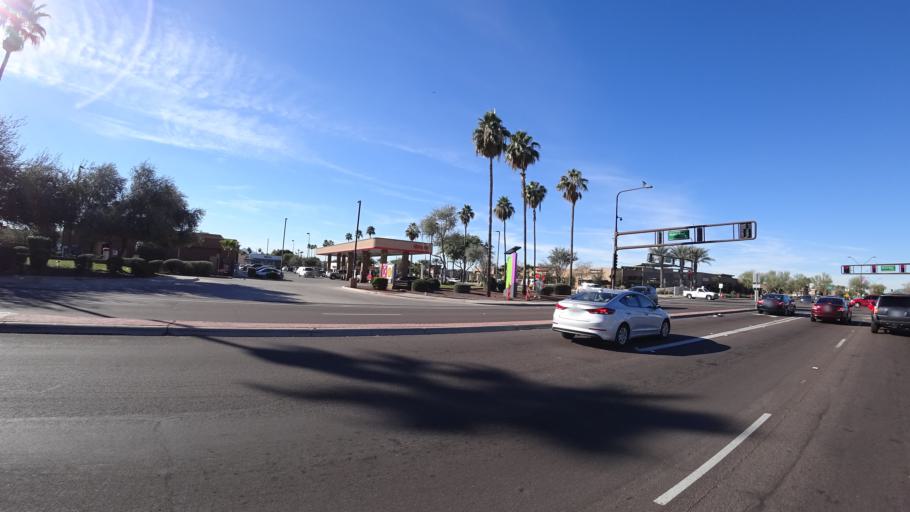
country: US
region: Arizona
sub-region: Maricopa County
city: Avondale
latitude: 33.4643
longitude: -112.3402
